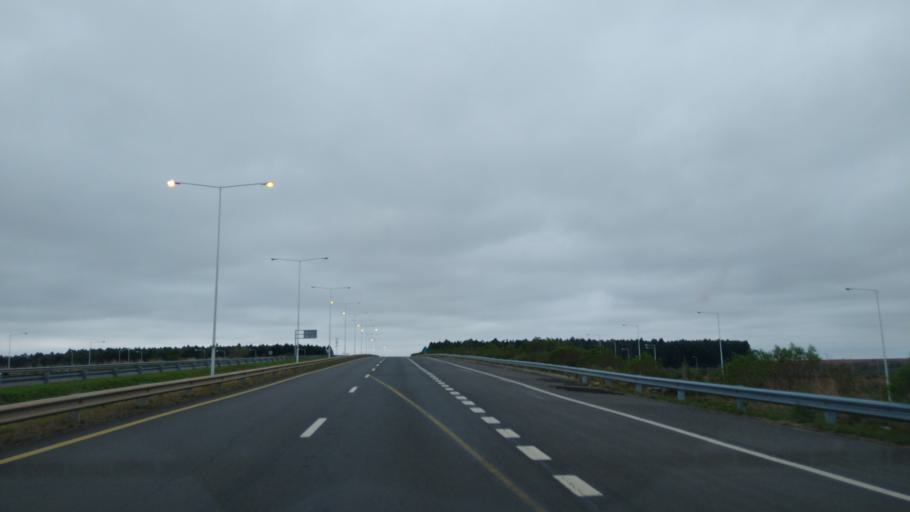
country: AR
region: Corrientes
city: Libertad
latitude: -30.0586
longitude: -57.8165
